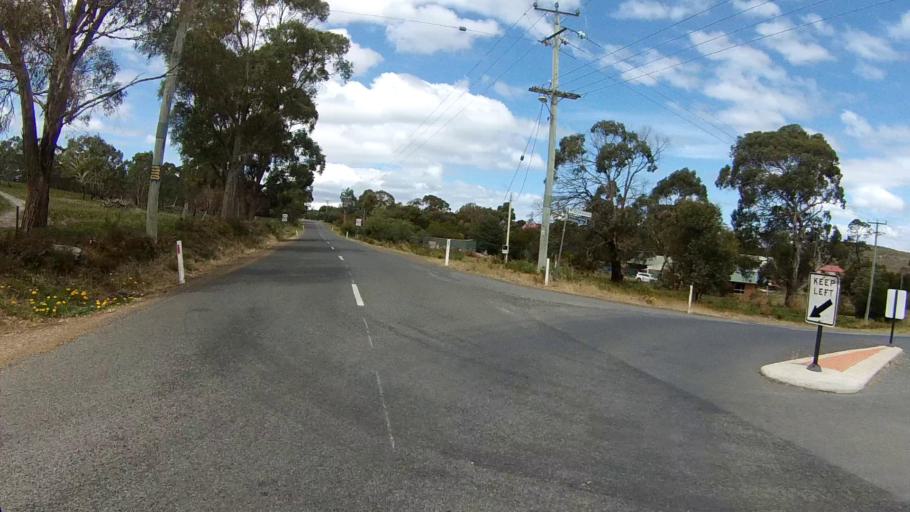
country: AU
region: Tasmania
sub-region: Sorell
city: Sorell
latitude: -42.8661
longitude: 147.6456
